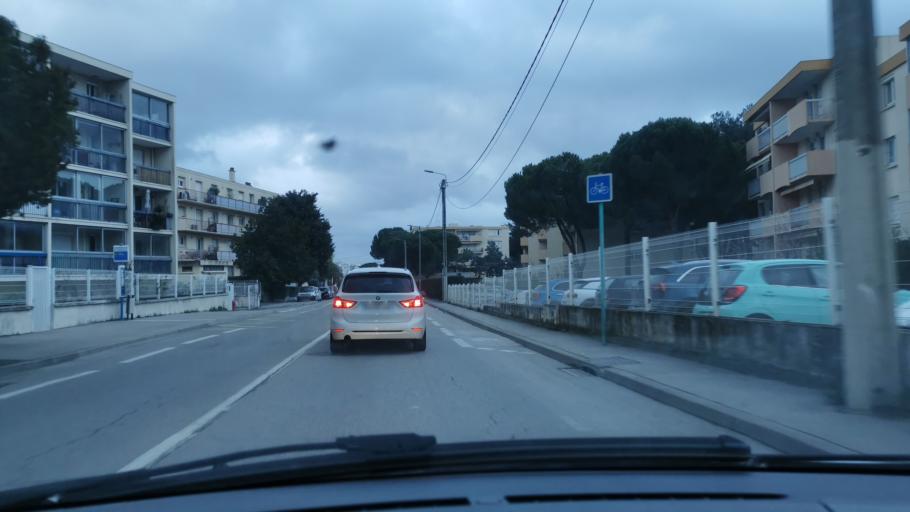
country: FR
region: Languedoc-Roussillon
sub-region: Departement de l'Herault
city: Montpellier
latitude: 43.5885
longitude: 3.8725
